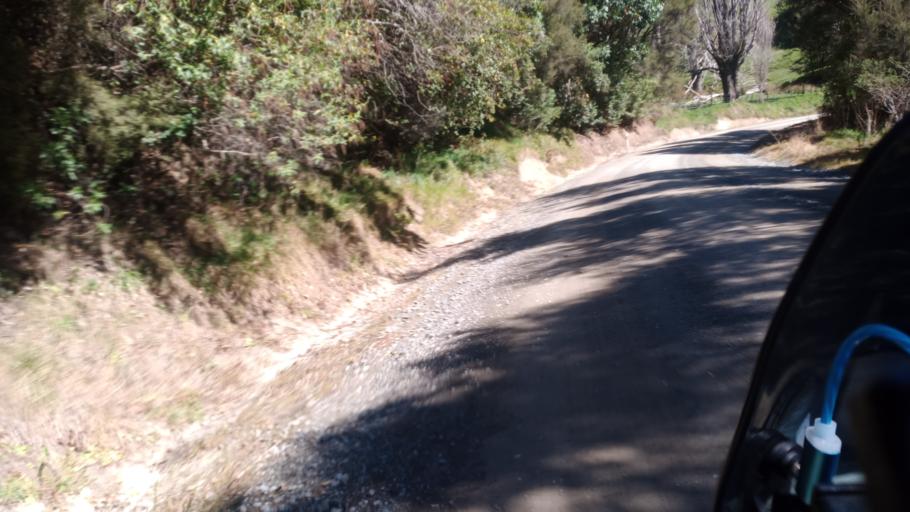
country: NZ
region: Gisborne
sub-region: Gisborne District
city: Gisborne
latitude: -37.9929
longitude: 178.3037
